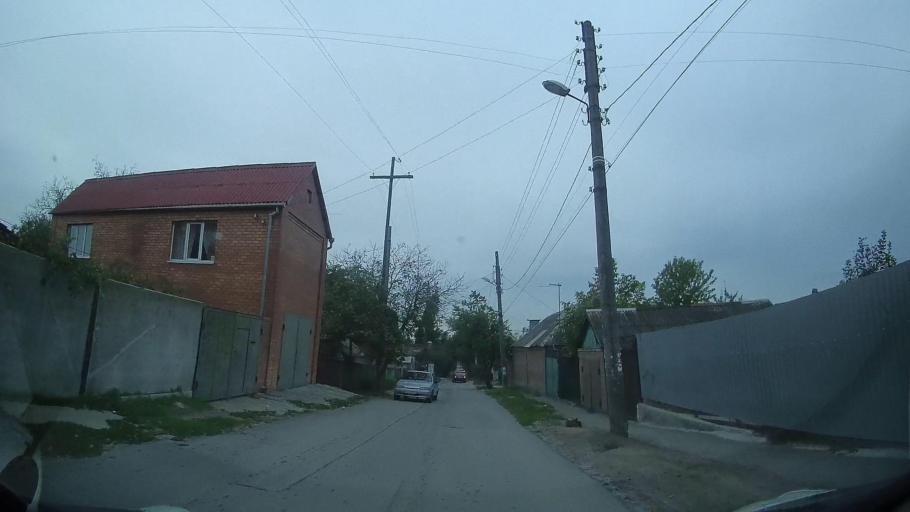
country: RU
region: Rostov
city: Severnyy
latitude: 47.2679
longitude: 39.6733
